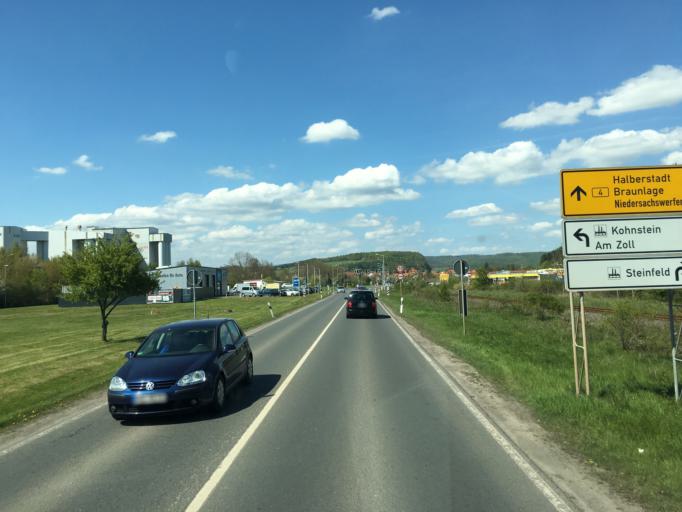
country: DE
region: Thuringia
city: Niedersachswerfen
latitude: 51.5368
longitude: 10.7698
